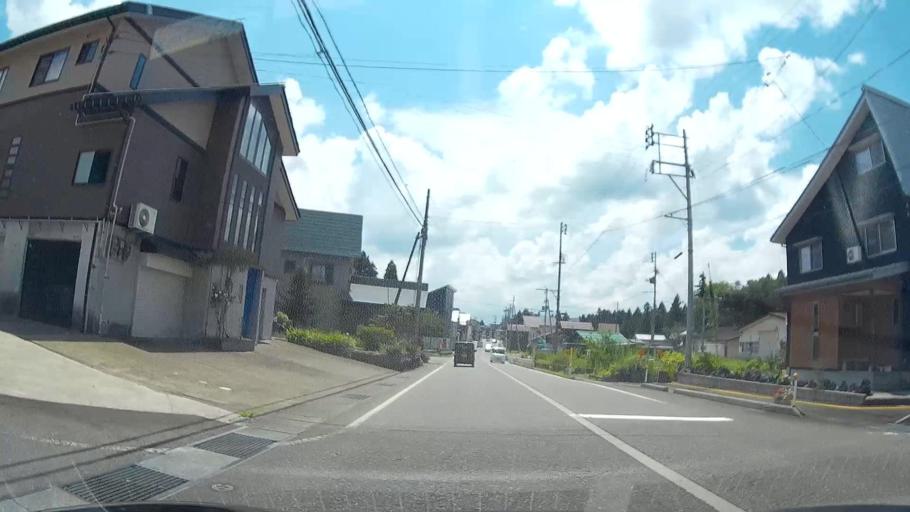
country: JP
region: Niigata
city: Tokamachi
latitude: 37.0785
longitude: 138.7188
